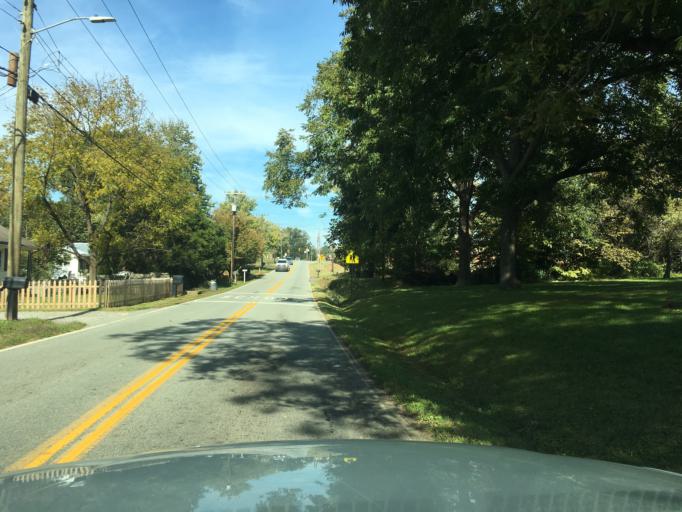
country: US
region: North Carolina
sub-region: Catawba County
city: Hickory
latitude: 35.7291
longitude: -81.2990
